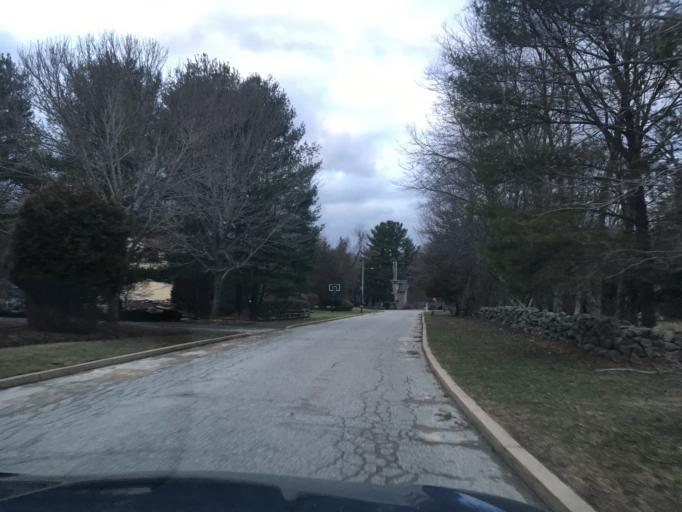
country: US
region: Rhode Island
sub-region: Washington County
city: Exeter
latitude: 41.6214
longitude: -71.5242
